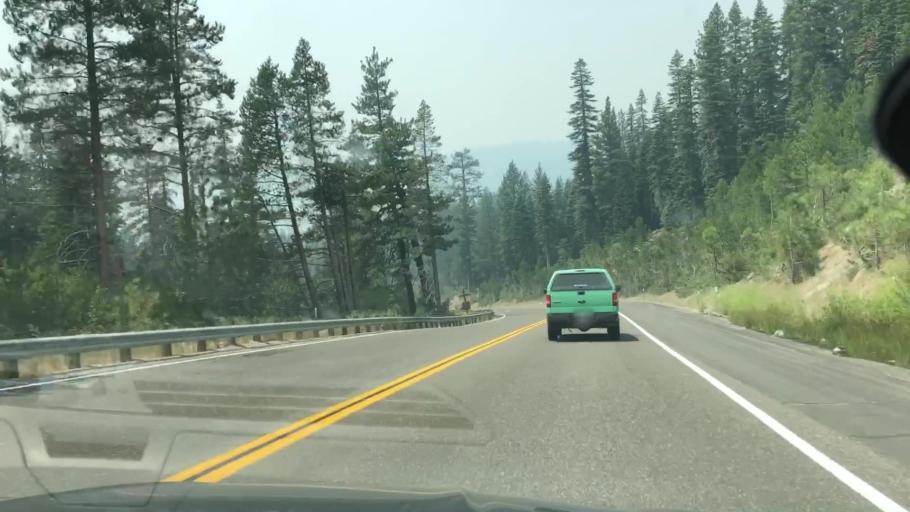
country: US
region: California
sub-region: El Dorado County
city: South Lake Tahoe
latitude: 38.8026
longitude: -120.1130
